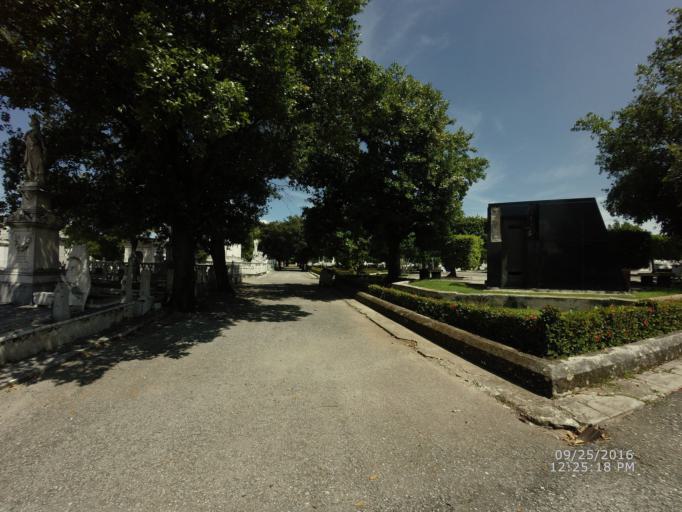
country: CU
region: La Habana
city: Havana
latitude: 23.1244
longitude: -82.3973
